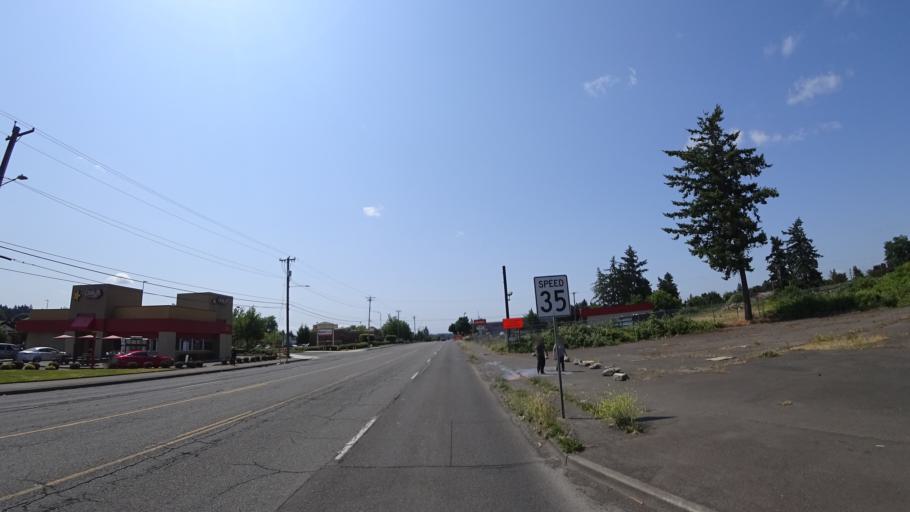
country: US
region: Oregon
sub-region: Multnomah County
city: Lents
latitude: 45.4503
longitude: -122.5792
